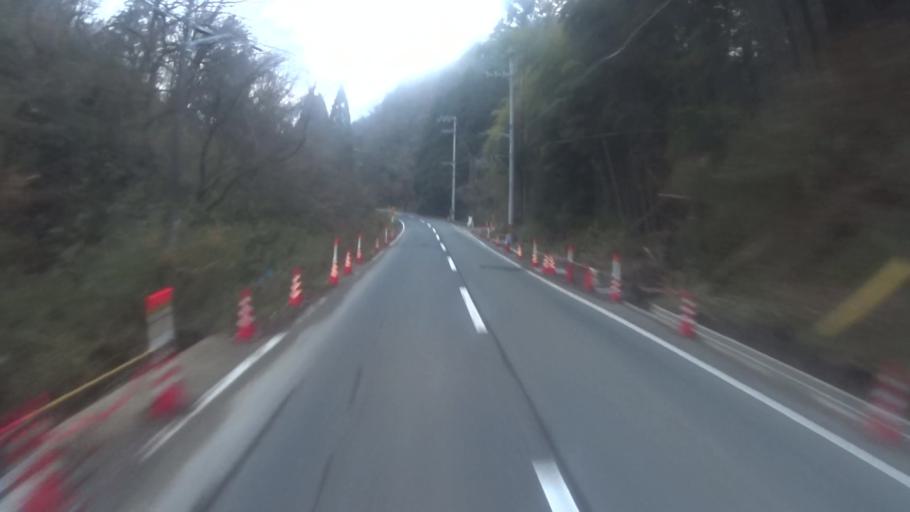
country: JP
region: Kyoto
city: Ayabe
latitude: 35.3168
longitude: 135.3169
